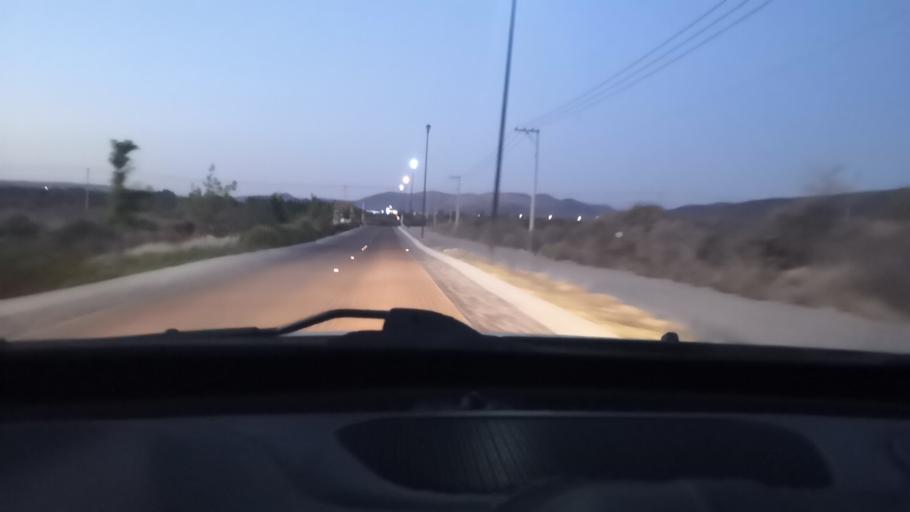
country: MX
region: Guanajuato
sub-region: Leon
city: Fraccionamiento Paseo de las Torres
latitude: 21.2343
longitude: -101.7919
